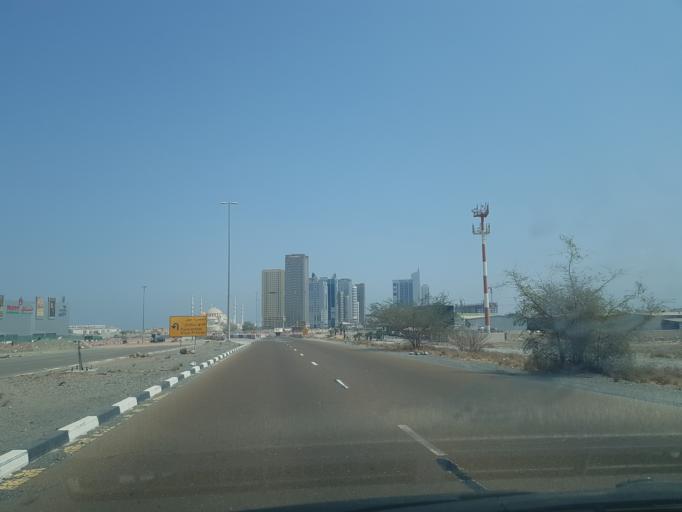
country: AE
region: Al Fujayrah
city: Al Fujayrah
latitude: 25.1211
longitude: 56.3136
